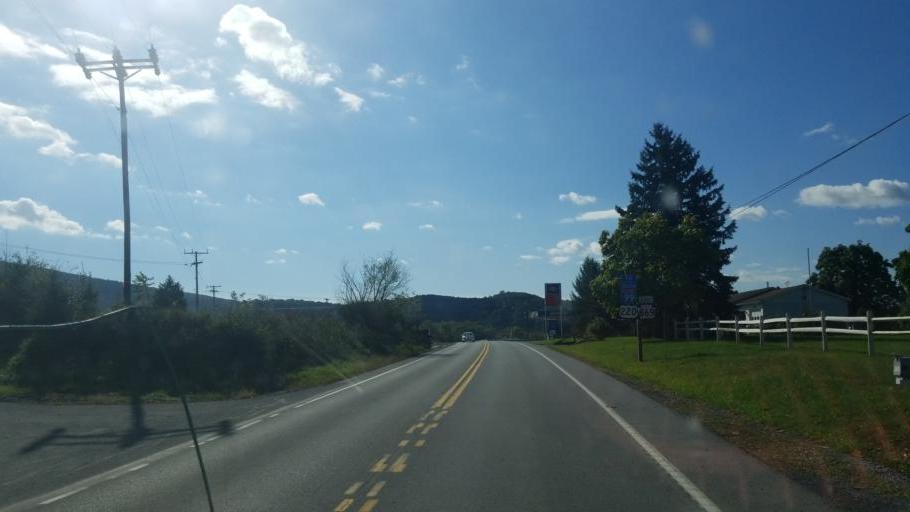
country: US
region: Pennsylvania
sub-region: Blair County
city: Claysburg
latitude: 40.1673
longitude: -78.5178
